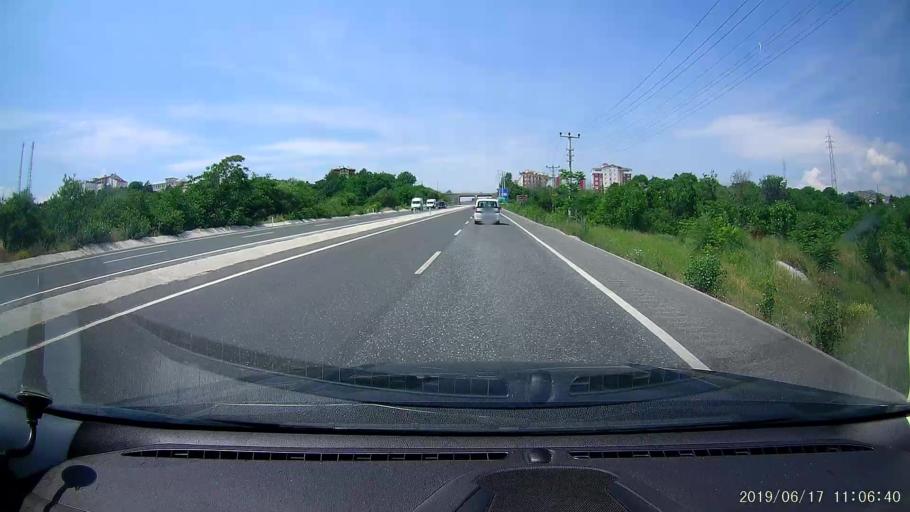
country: TR
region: Kastamonu
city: Tosya
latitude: 41.0109
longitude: 34.0639
